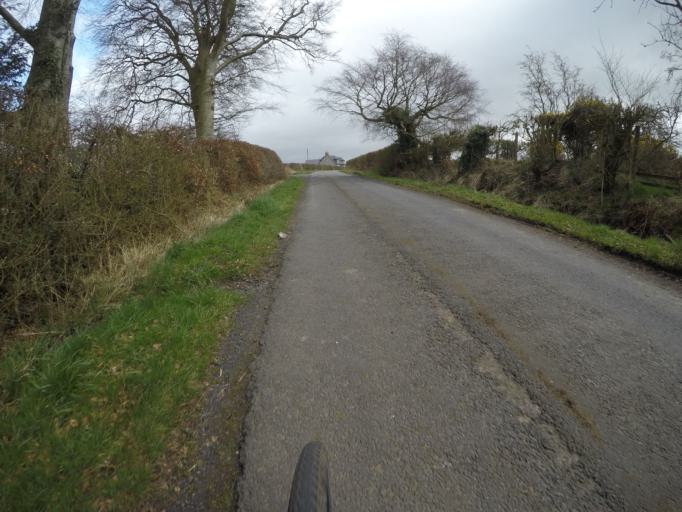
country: GB
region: Scotland
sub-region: East Ayrshire
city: Kilmaurs
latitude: 55.6714
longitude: -4.5657
